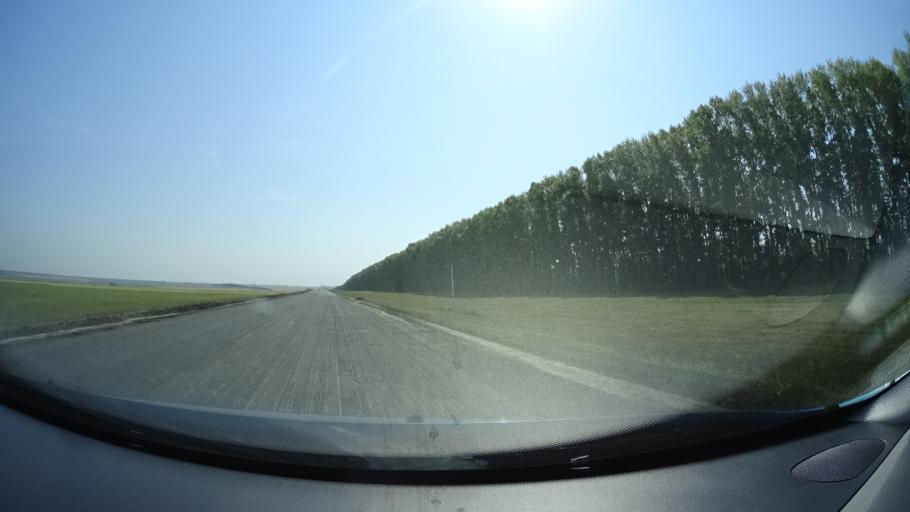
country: RU
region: Bashkortostan
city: Kabakovo
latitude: 54.4493
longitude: 55.9779
